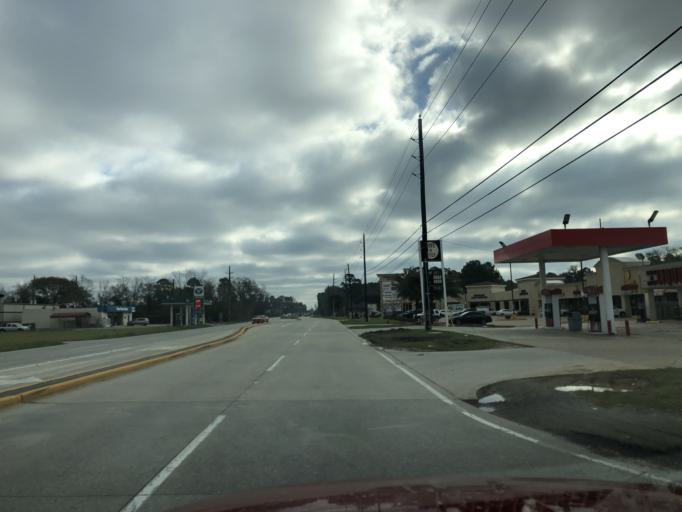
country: US
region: Texas
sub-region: Harris County
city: Spring
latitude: 30.0826
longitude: -95.4690
